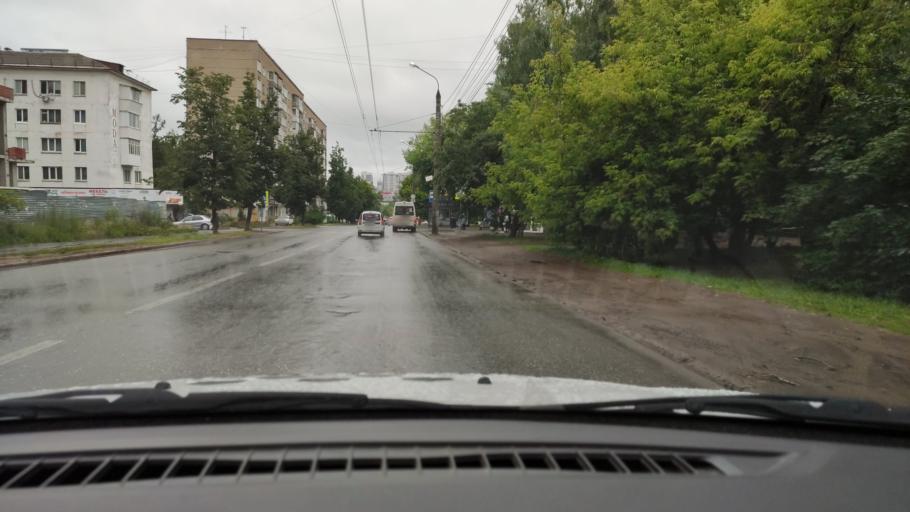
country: RU
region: Udmurtiya
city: Izhevsk
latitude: 56.8766
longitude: 53.1897
